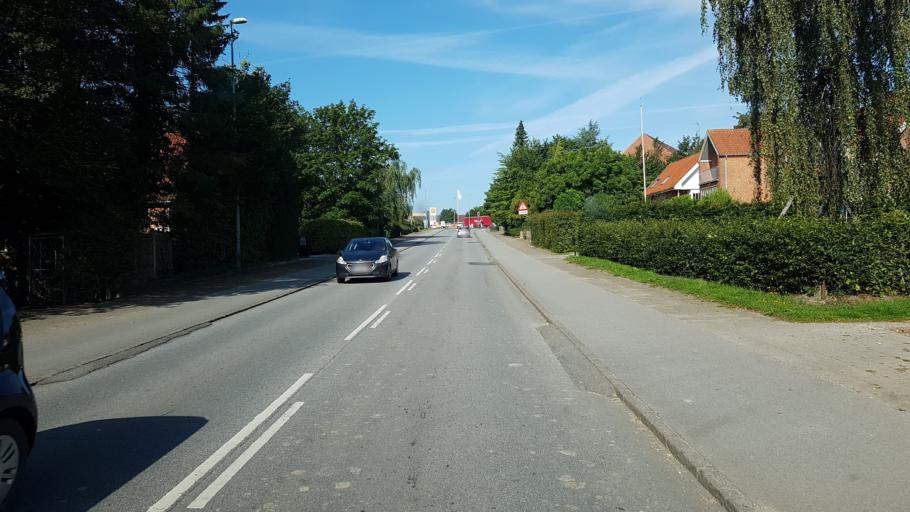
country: DK
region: South Denmark
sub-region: Haderslev Kommune
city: Haderslev
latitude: 55.2438
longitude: 9.5067
